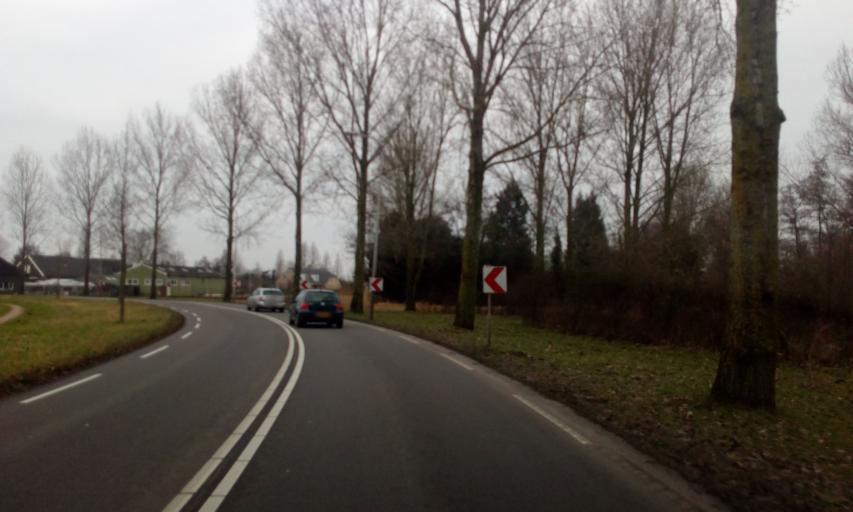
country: NL
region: South Holland
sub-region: Gemeente Gouda
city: Gouda
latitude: 52.0251
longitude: 4.7263
